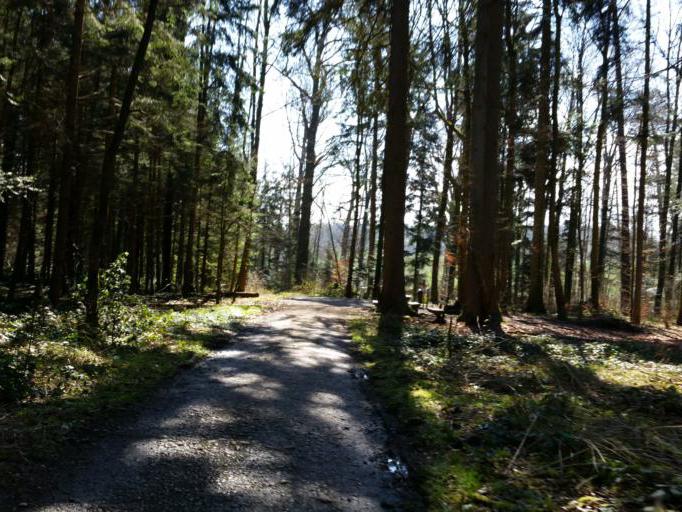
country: CH
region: Thurgau
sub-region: Arbon District
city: Amriswil
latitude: 47.5445
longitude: 9.3209
